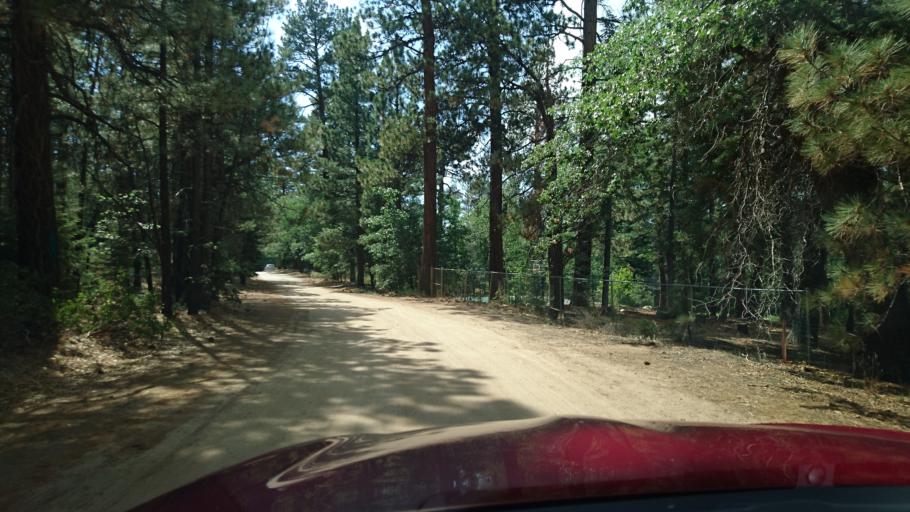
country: US
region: California
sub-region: San Bernardino County
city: Big Bear Lake
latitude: 34.2359
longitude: -116.8812
